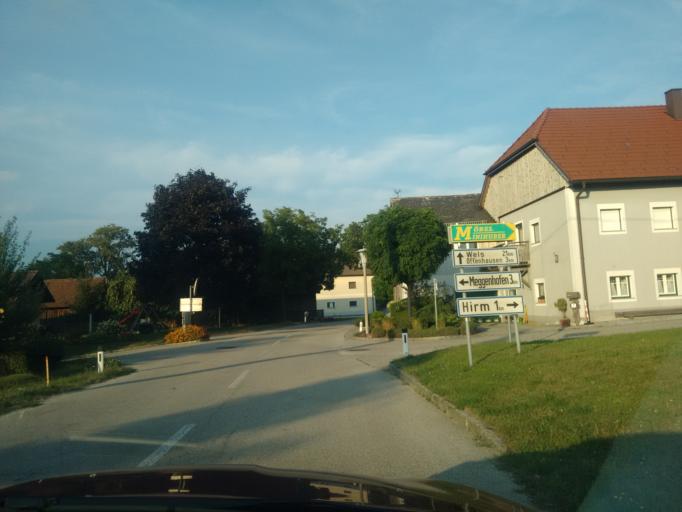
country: AT
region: Upper Austria
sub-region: Wels-Land
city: Offenhausen
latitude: 48.1580
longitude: 13.7996
